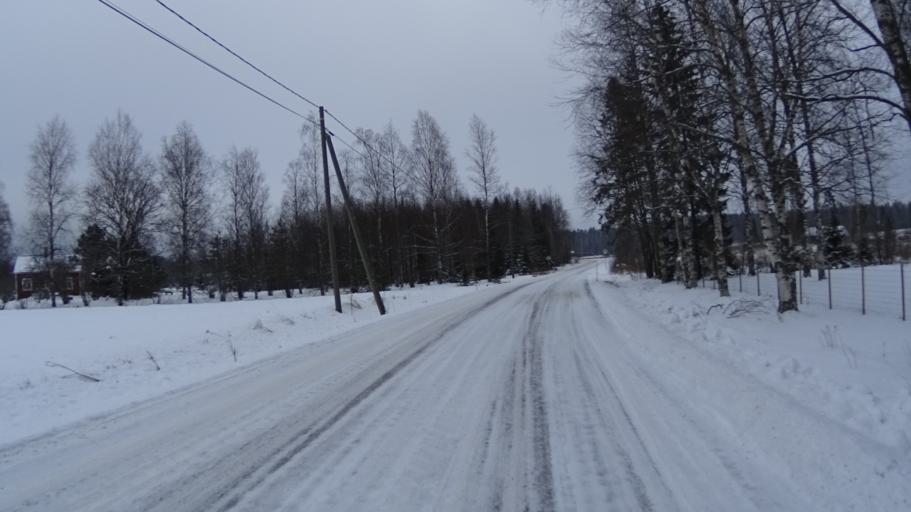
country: FI
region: Uusimaa
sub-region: Helsinki
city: Karkkila
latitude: 60.4554
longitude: 24.1310
